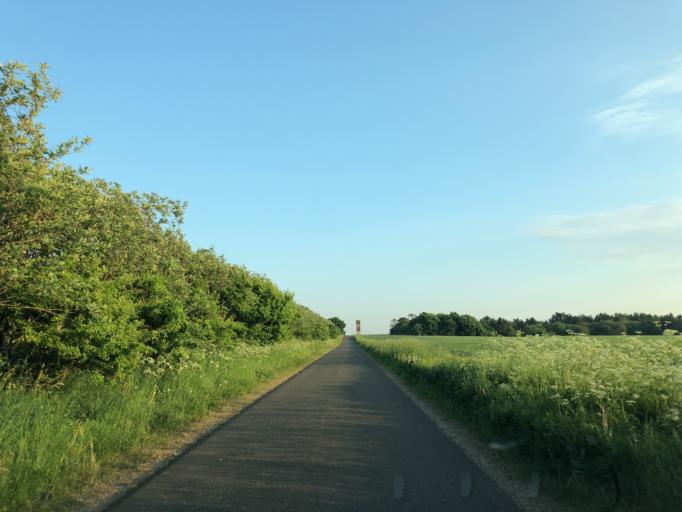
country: DK
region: Central Jutland
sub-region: Struer Kommune
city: Struer
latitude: 56.4124
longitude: 8.4886
